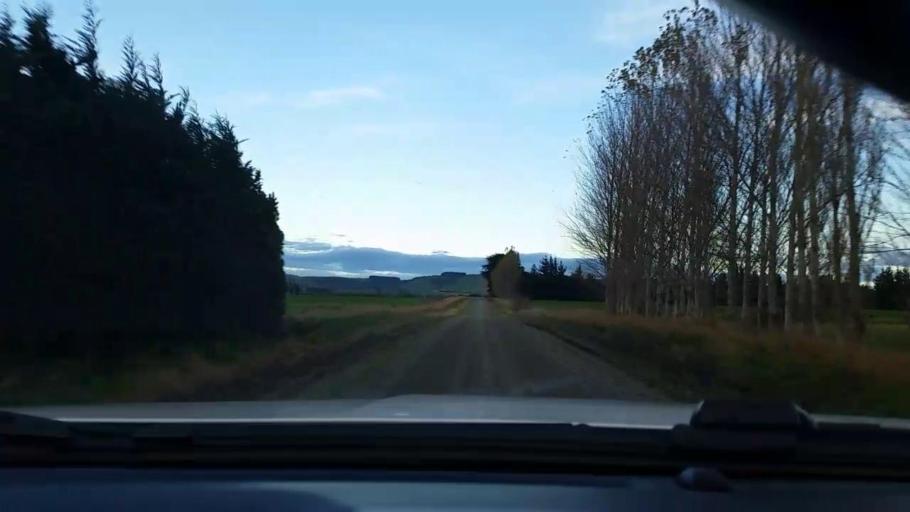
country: NZ
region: Southland
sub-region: Southland District
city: Winton
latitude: -46.1047
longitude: 168.4567
